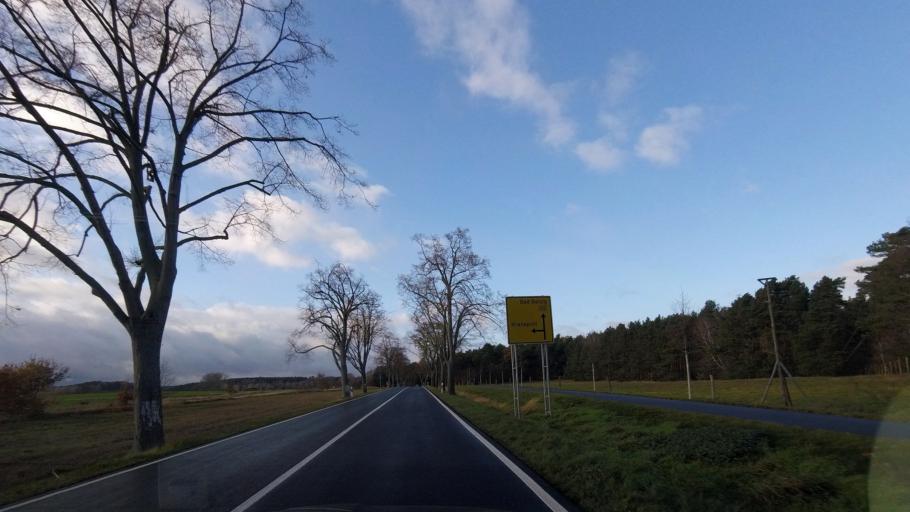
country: DE
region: Brandenburg
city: Belzig
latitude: 52.1272
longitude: 12.6343
